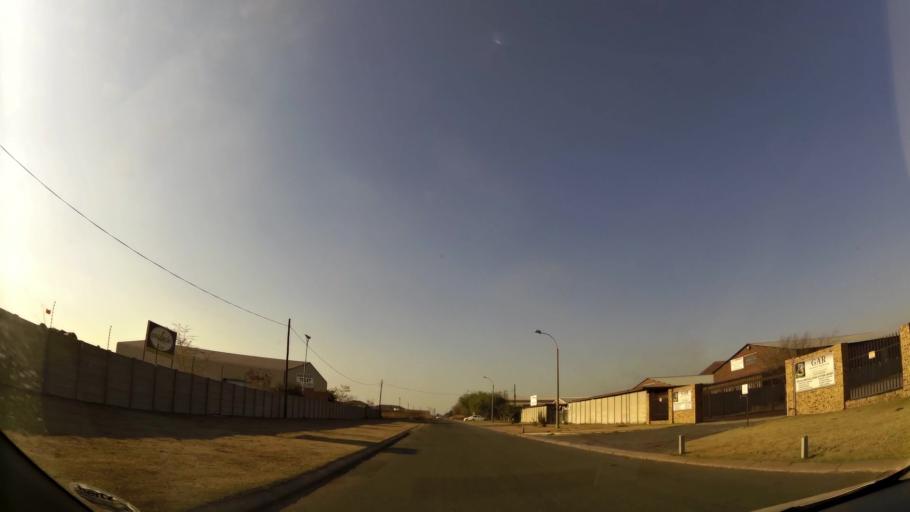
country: ZA
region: Gauteng
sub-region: West Rand District Municipality
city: Randfontein
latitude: -26.1977
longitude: 27.6906
